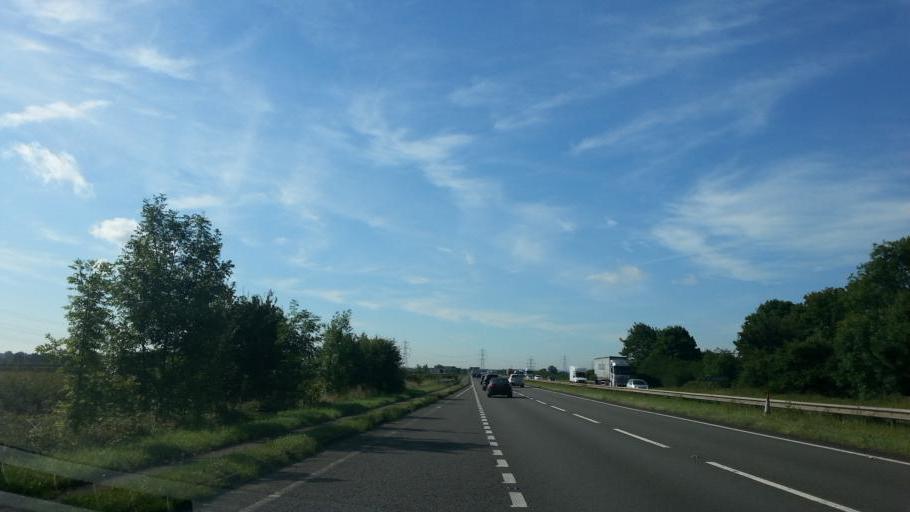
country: GB
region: England
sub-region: Lincolnshire
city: Long Bennington
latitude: 53.0289
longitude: -0.7698
